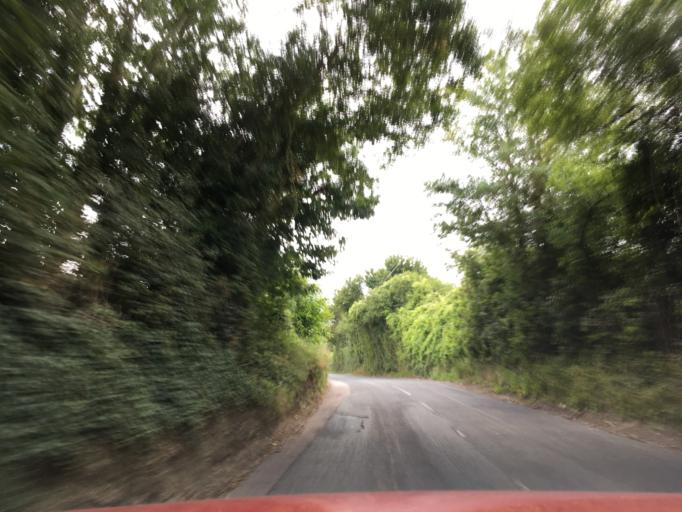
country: GB
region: England
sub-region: Kent
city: Yalding
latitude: 51.2405
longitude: 0.4492
